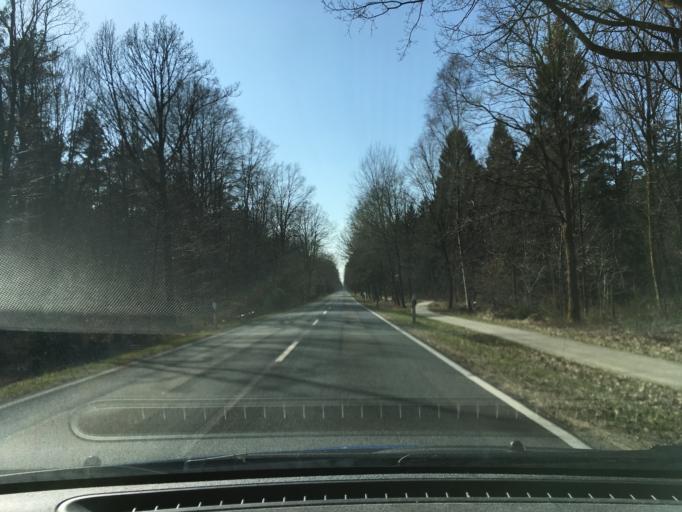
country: DE
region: Lower Saxony
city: Unterluss
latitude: 52.8318
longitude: 10.2710
